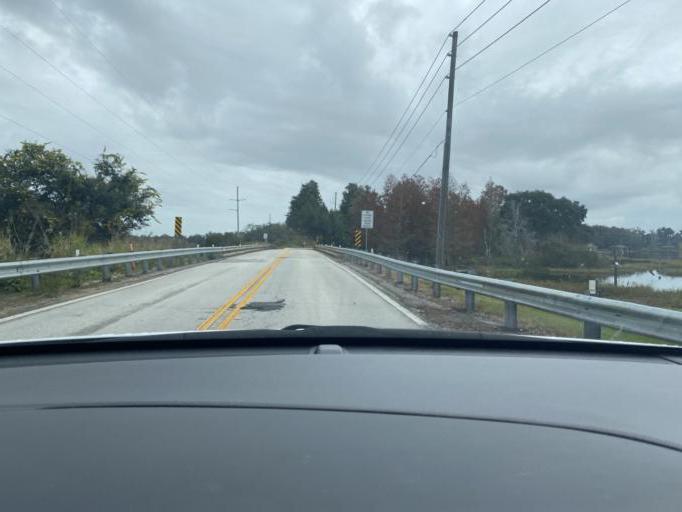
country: US
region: Florida
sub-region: Lake County
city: Clermont
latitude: 28.5807
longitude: -81.7873
